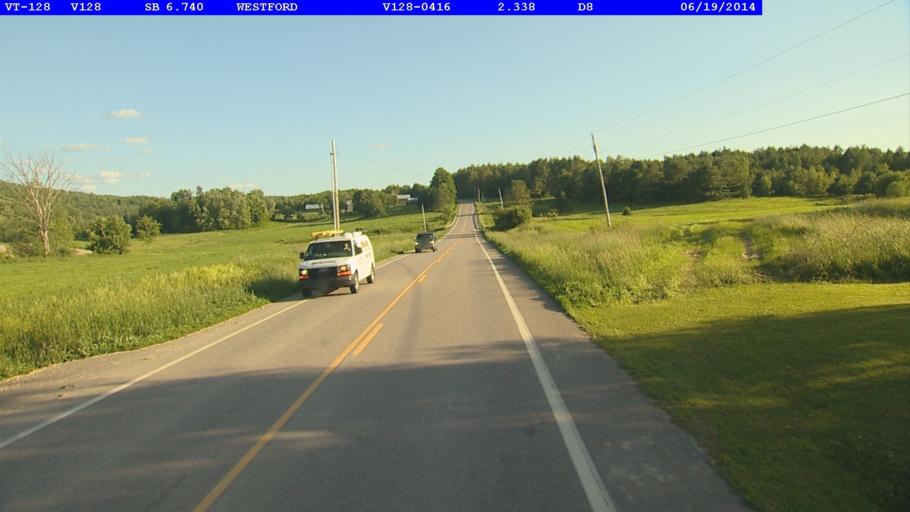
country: US
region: Vermont
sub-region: Chittenden County
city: Jericho
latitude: 44.5910
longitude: -73.0135
